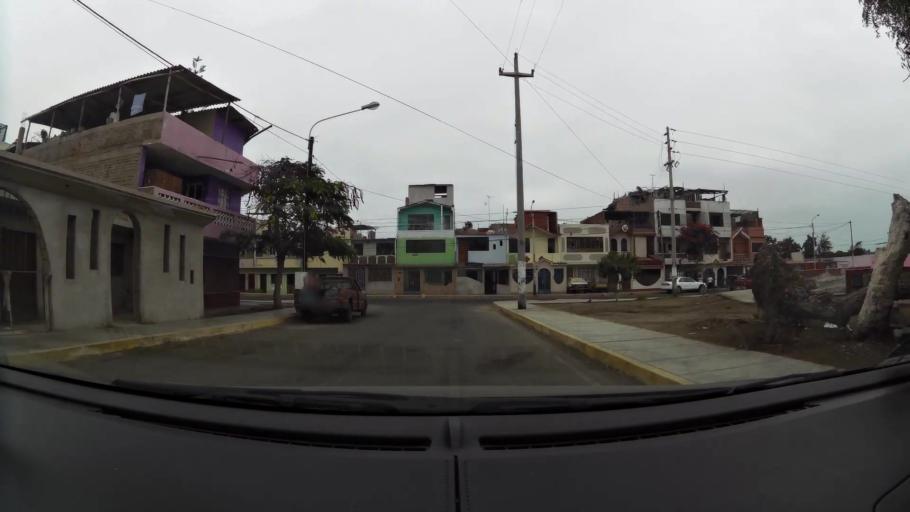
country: PE
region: Ancash
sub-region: Provincia de Santa
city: Chimbote
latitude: -9.0713
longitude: -78.5980
